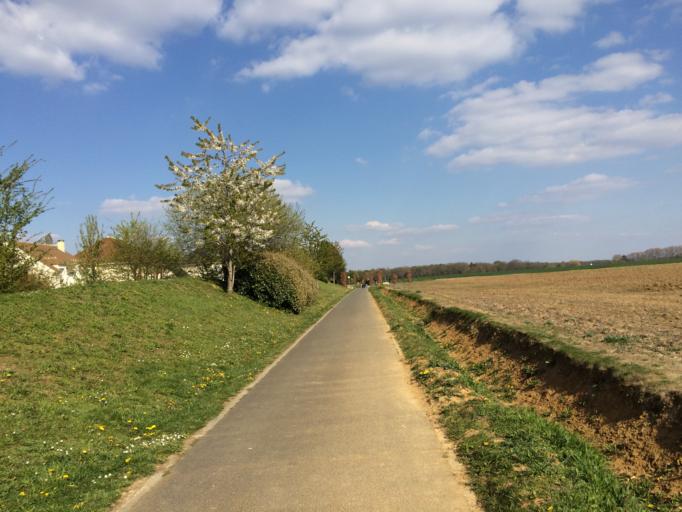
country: FR
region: Ile-de-France
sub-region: Departement des Yvelines
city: Jouy-en-Josas
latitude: 48.7512
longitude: 2.1825
